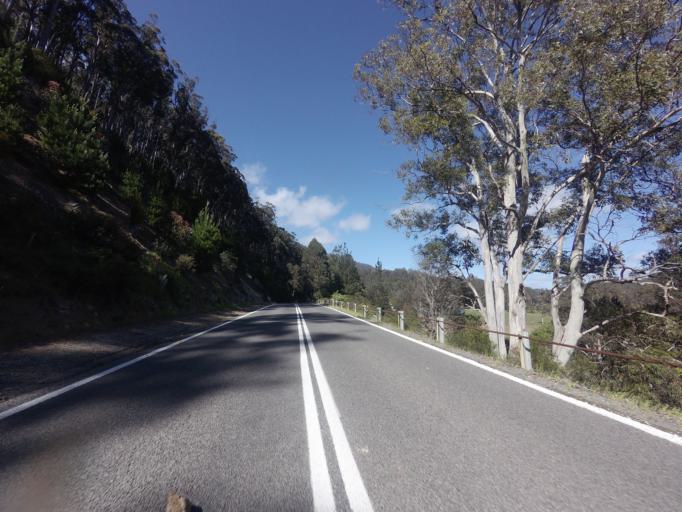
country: AU
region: Tasmania
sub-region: Derwent Valley
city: New Norfolk
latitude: -42.7102
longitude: 146.7058
